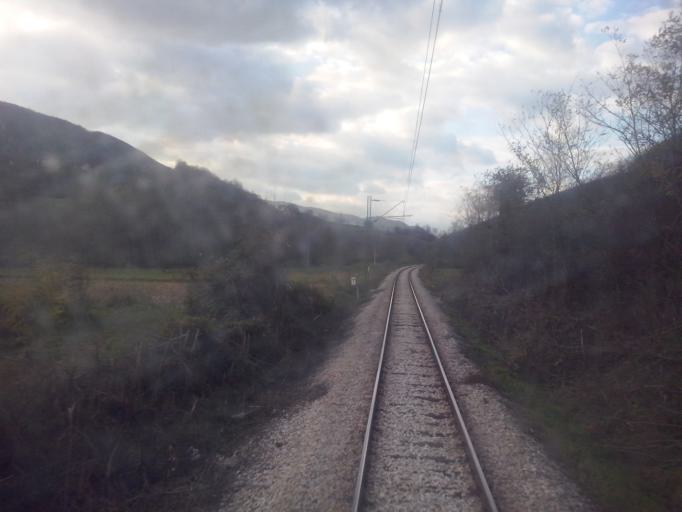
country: RS
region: Central Serbia
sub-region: Zlatiborski Okrug
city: Kosjeric
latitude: 43.9790
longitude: 19.9459
